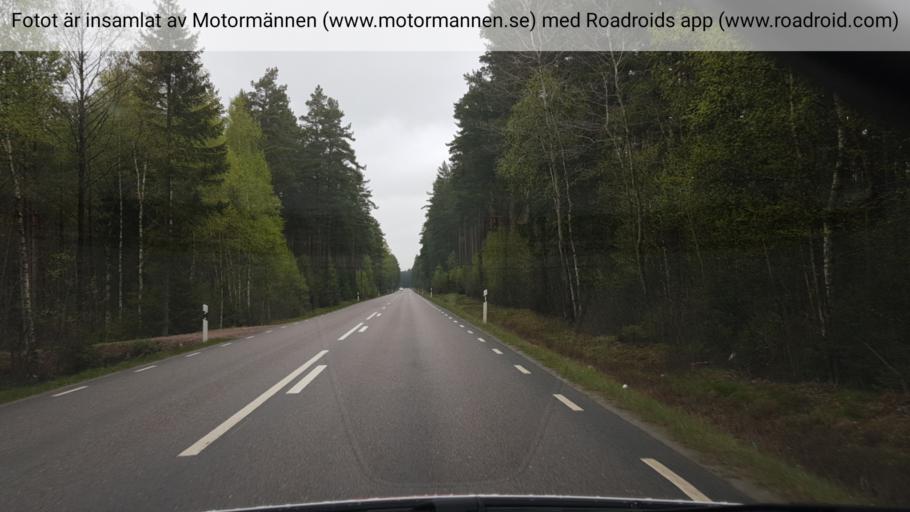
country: SE
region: Vaestra Goetaland
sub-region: Skovde Kommun
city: Stopen
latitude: 58.4569
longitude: 13.9558
